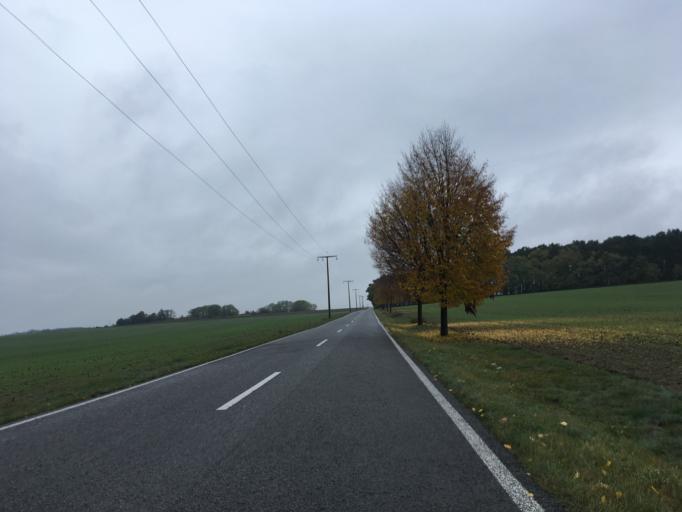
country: DE
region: Brandenburg
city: Friedland
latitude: 52.0625
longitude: 14.1881
